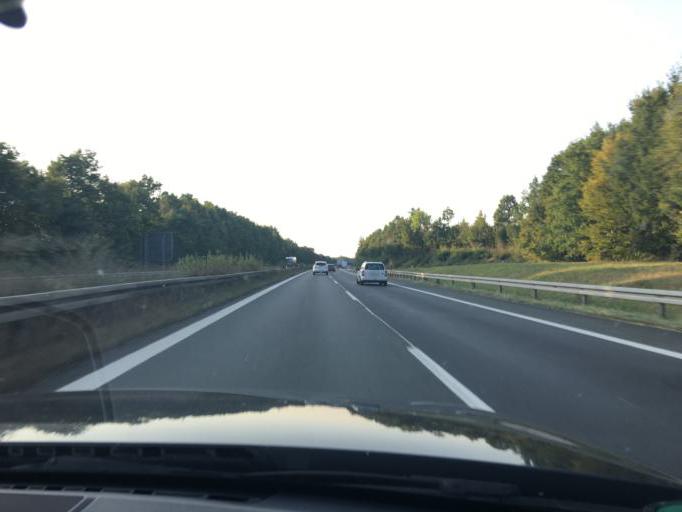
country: DE
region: Bavaria
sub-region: Upper Franconia
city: Buttenheim
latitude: 49.7952
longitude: 11.0253
